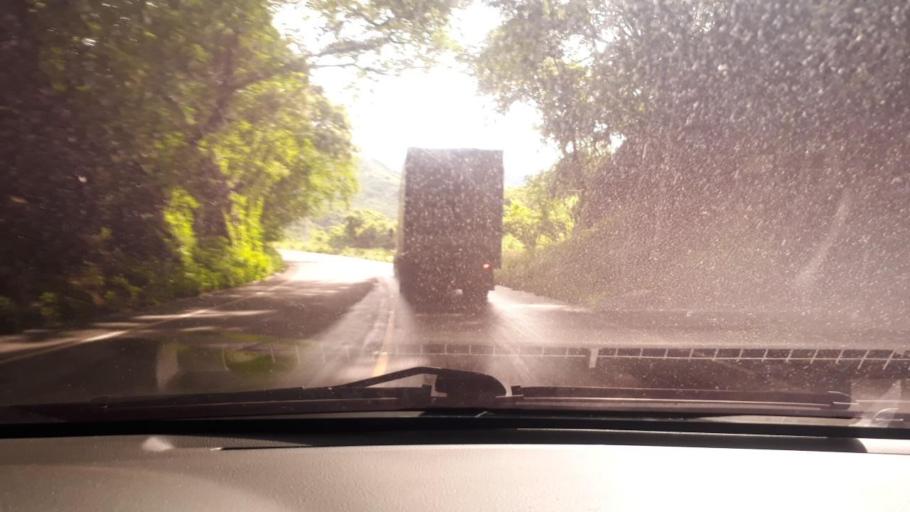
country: GT
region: Jutiapa
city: Pasaco
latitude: 13.9012
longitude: -90.1755
